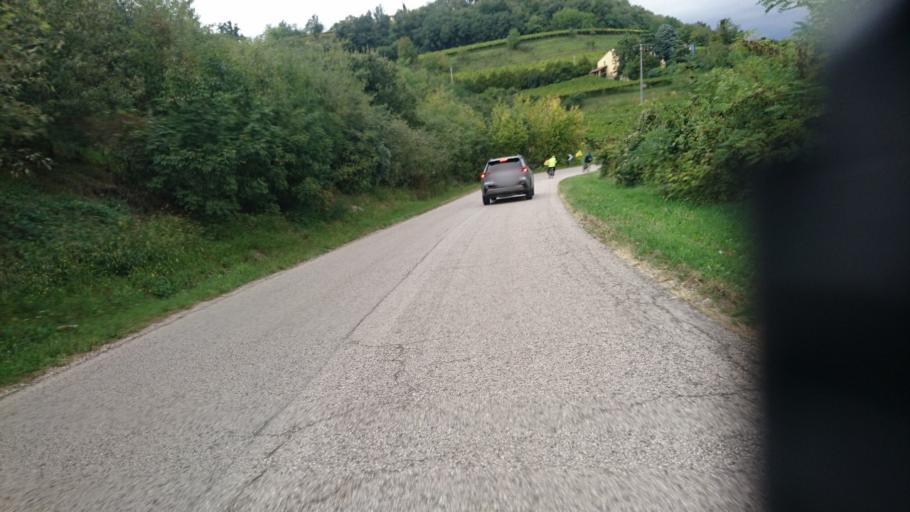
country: IT
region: Veneto
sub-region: Provincia di Vicenza
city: Gambellara
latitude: 45.4508
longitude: 11.3569
